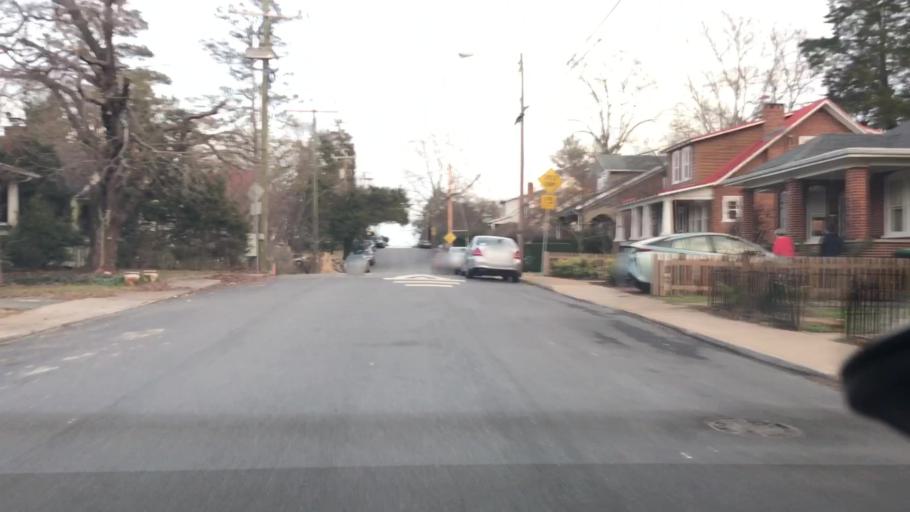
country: US
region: Virginia
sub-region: City of Charlottesville
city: Charlottesville
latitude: 38.0244
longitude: -78.5143
